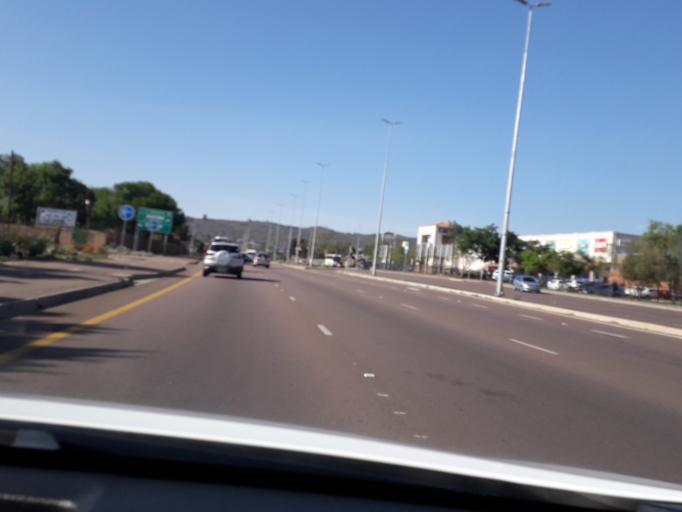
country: ZA
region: Gauteng
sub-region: City of Tshwane Metropolitan Municipality
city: Pretoria
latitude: -25.7564
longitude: 28.3238
